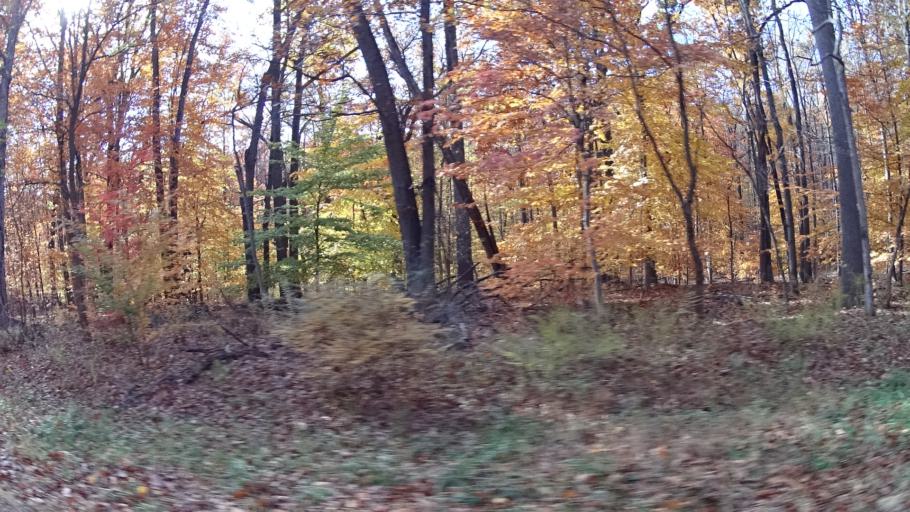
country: US
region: New Jersey
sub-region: Somerset County
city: Bernardsville
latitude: 40.7580
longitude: -74.5394
